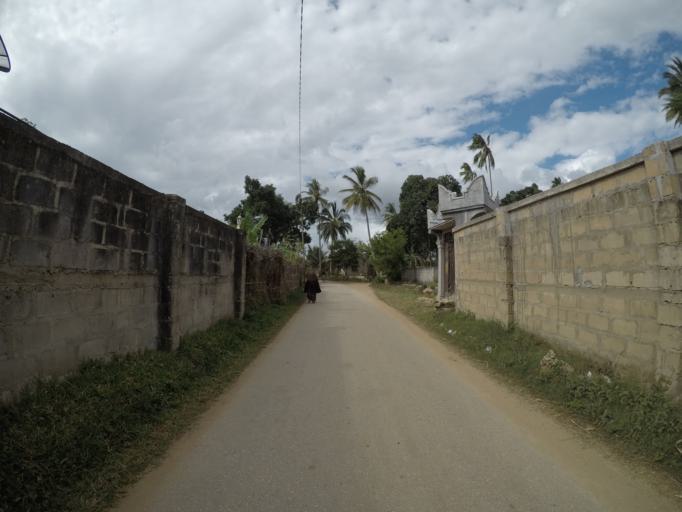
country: TZ
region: Zanzibar Central/South
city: Koani
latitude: -6.1937
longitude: 39.2644
